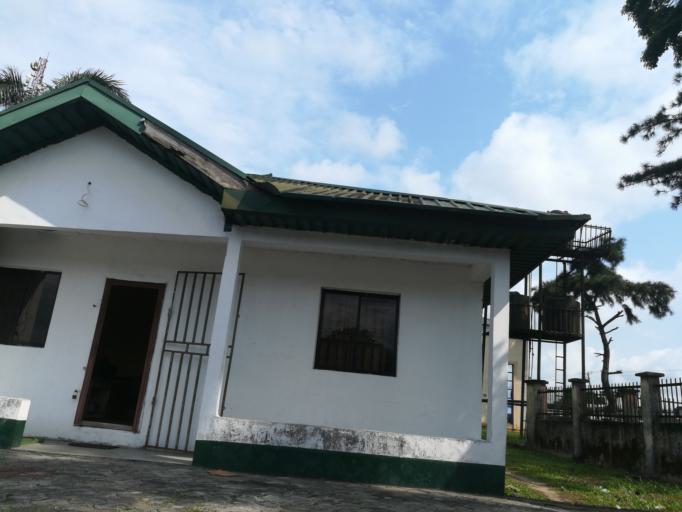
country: NG
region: Rivers
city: Okrika
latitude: 4.7524
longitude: 7.0992
